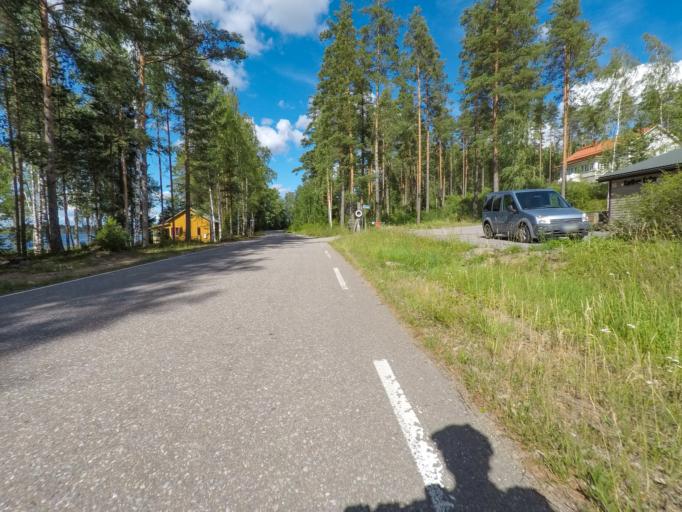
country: FI
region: South Karelia
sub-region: Lappeenranta
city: Joutseno
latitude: 61.1166
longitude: 28.3747
